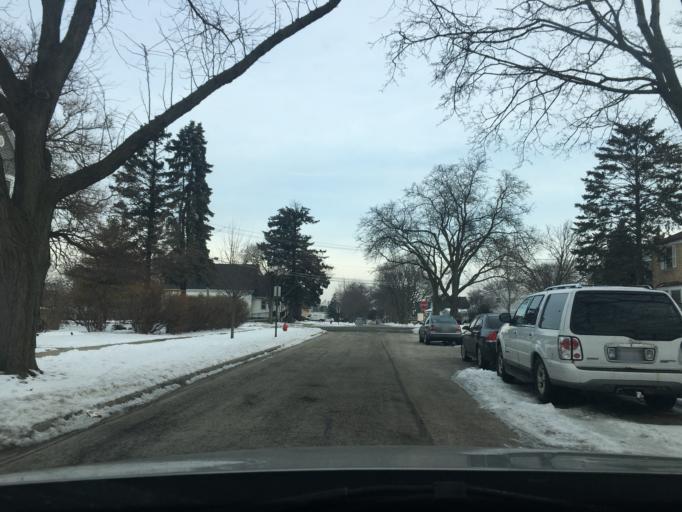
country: US
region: Illinois
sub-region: Cook County
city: Des Plaines
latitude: 42.0199
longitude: -87.8869
